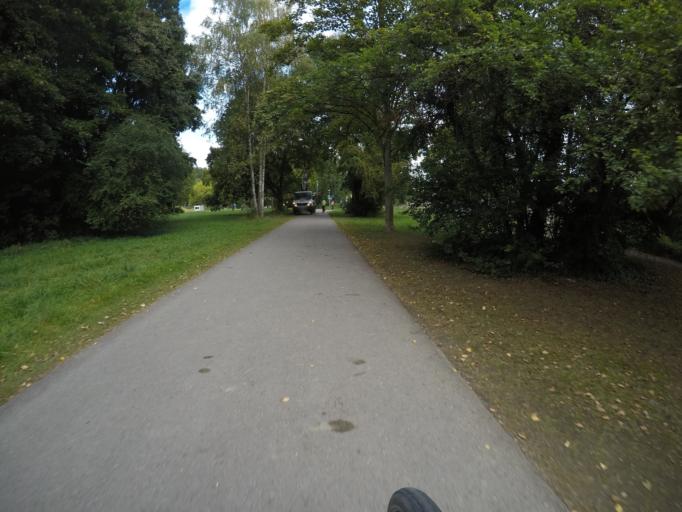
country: DE
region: Baden-Wuerttemberg
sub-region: Regierungsbezirk Stuttgart
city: Freiberg am Neckar
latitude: 48.9106
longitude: 9.2166
